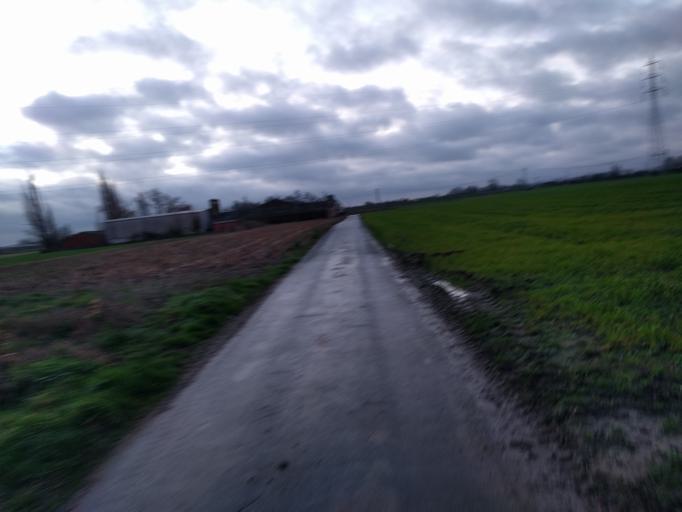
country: BE
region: Flanders
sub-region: Provincie West-Vlaanderen
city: Wevelgem
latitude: 50.8293
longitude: 3.1607
